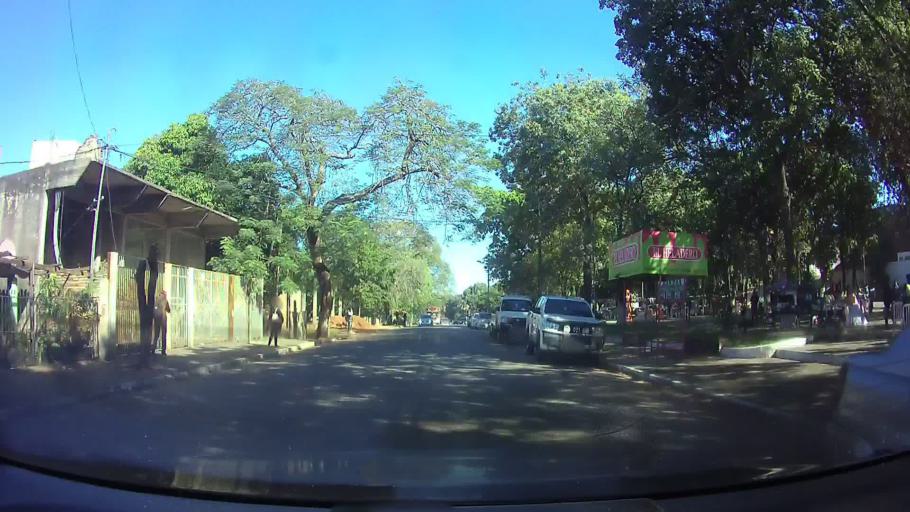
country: PY
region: Central
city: Villa Elisa
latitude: -25.3765
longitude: -57.5810
